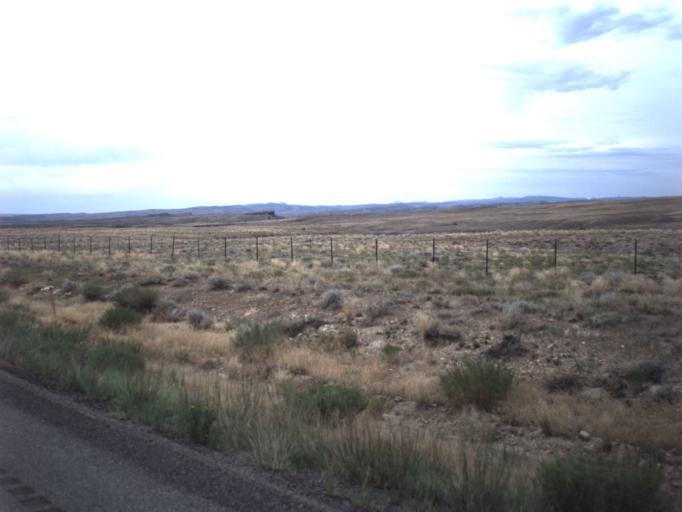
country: US
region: Utah
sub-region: Carbon County
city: East Carbon City
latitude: 39.3876
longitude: -110.4121
